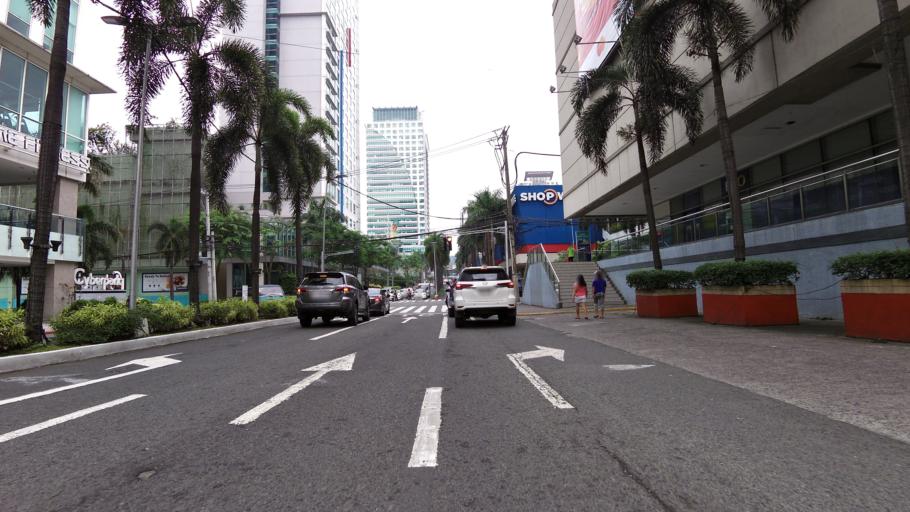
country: PH
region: Metro Manila
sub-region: San Juan
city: San Juan
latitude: 14.6194
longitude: 121.0549
